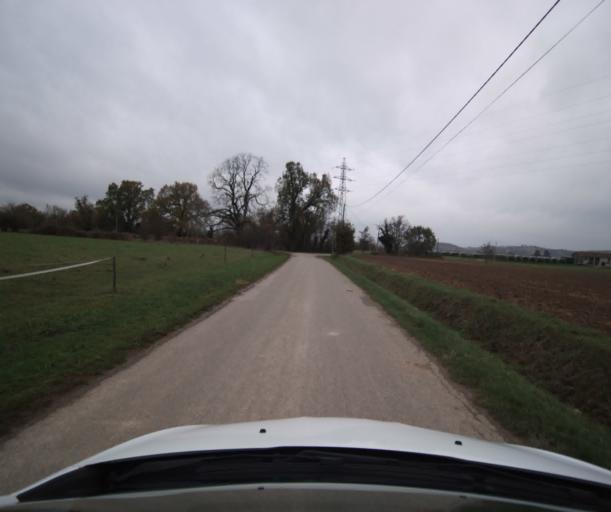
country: FR
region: Midi-Pyrenees
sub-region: Departement du Tarn-et-Garonne
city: Moissac
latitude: 44.0965
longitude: 1.1573
